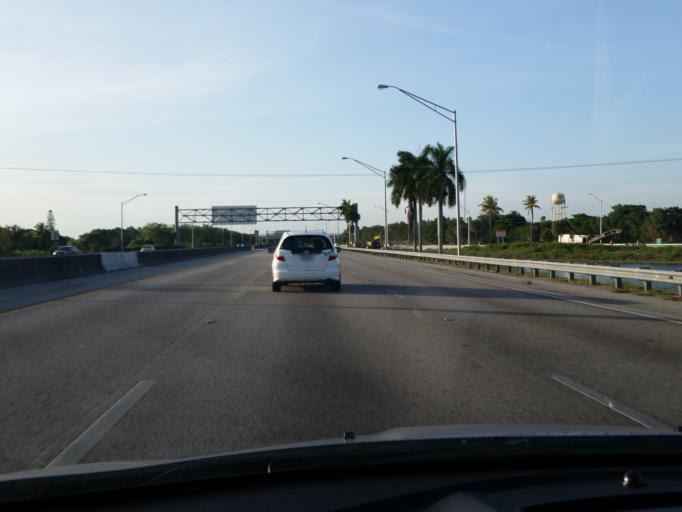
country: US
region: Florida
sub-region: Broward County
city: Miramar
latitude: 25.9760
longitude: -80.2298
